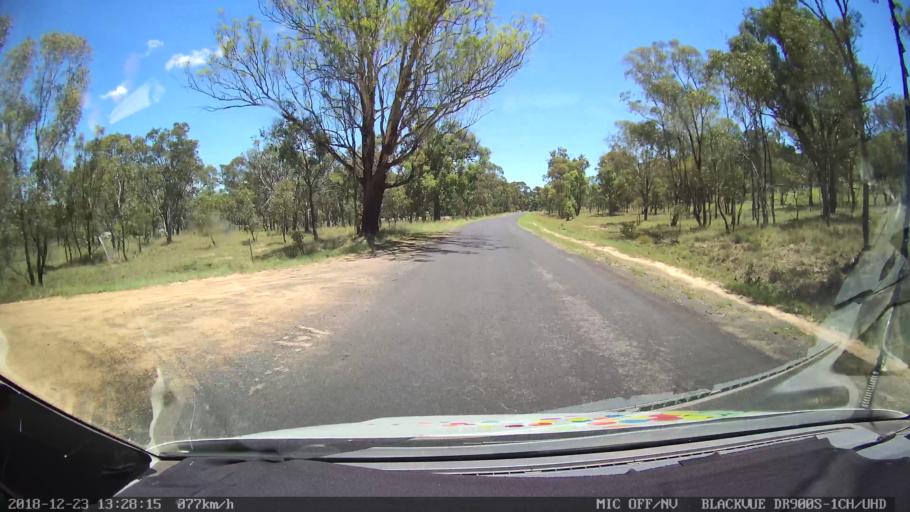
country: AU
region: New South Wales
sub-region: Armidale Dumaresq
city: Armidale
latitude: -30.4655
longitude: 151.3510
